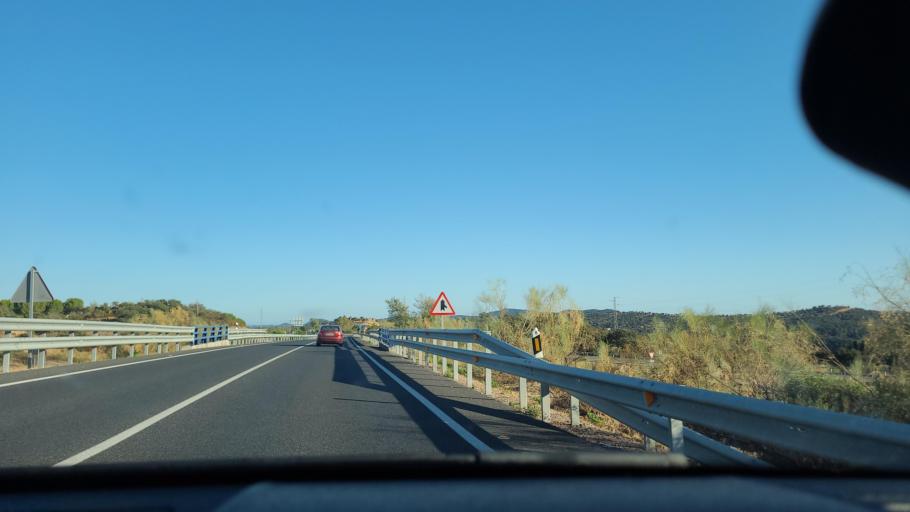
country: ES
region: Andalusia
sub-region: Province of Cordoba
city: Villaharta
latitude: 38.0967
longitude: -4.8712
